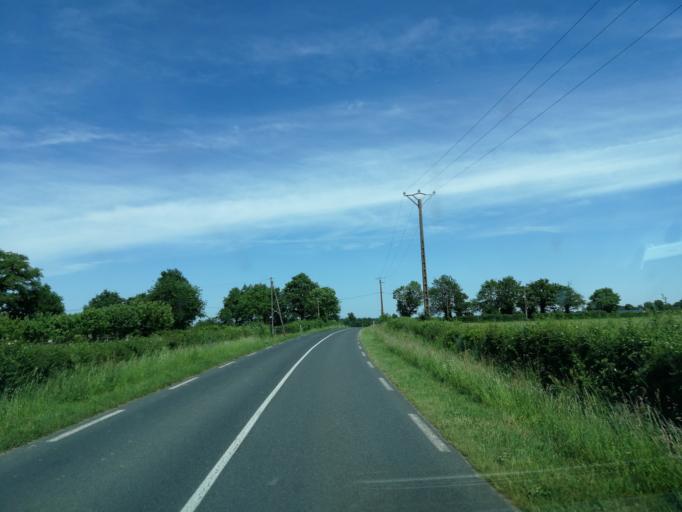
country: FR
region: Poitou-Charentes
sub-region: Departement des Deux-Sevres
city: Bressuire
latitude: 46.8208
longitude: -0.5243
